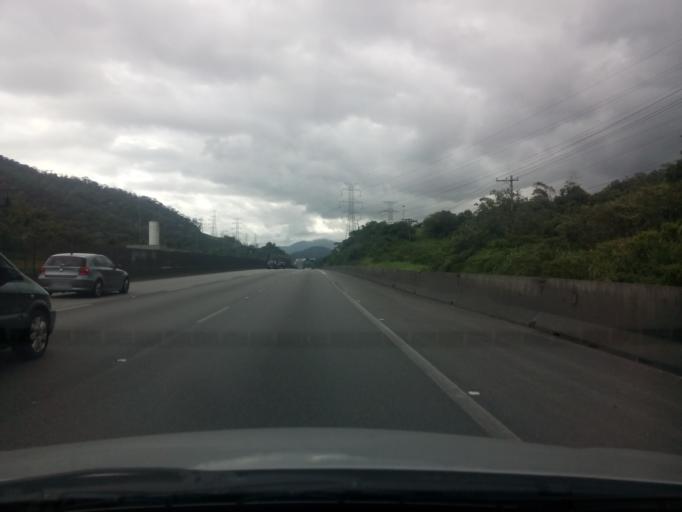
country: BR
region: Sao Paulo
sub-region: Cubatao
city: Cubatao
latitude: -23.8507
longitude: -46.4041
